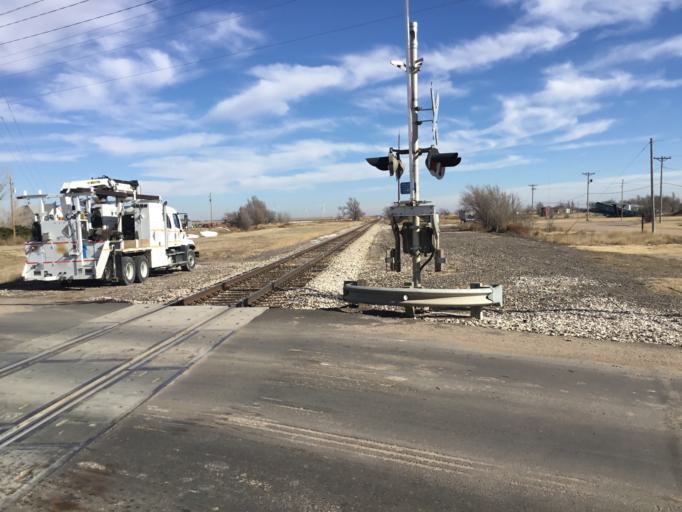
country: US
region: Kansas
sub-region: Ford County
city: Dodge City
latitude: 37.4446
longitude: -100.0153
